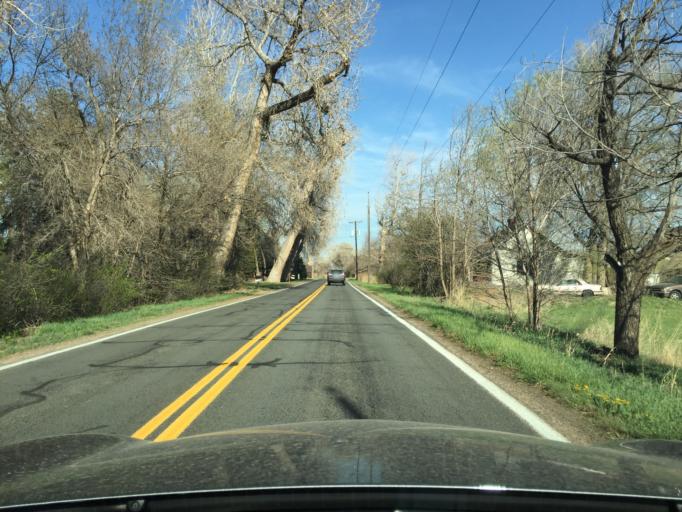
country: US
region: Colorado
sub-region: Boulder County
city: Erie
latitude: 40.0549
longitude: -105.0825
